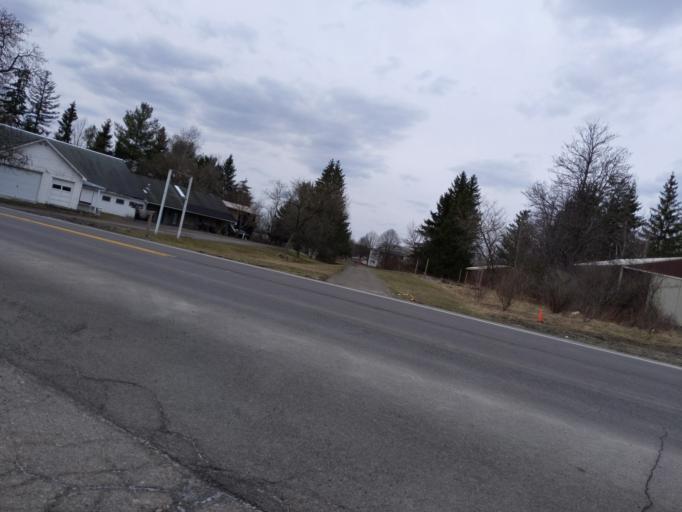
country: US
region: New York
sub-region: Tompkins County
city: Dryden
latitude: 42.5127
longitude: -76.3439
